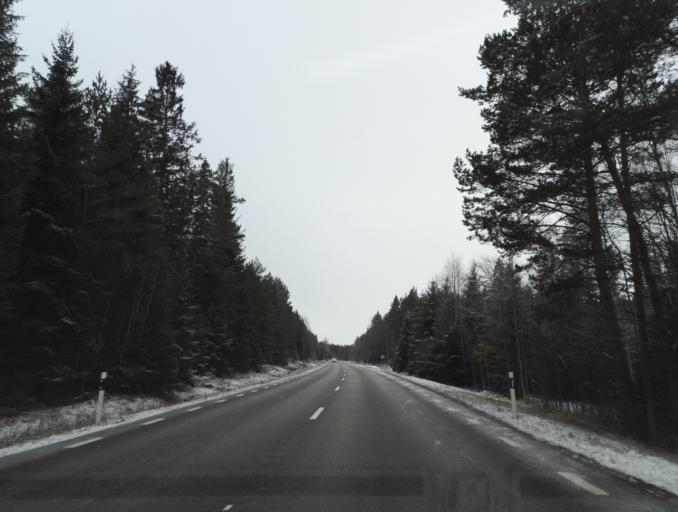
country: SE
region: Kronoberg
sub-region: Uppvidinge Kommun
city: Aseda
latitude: 57.1760
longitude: 15.4954
